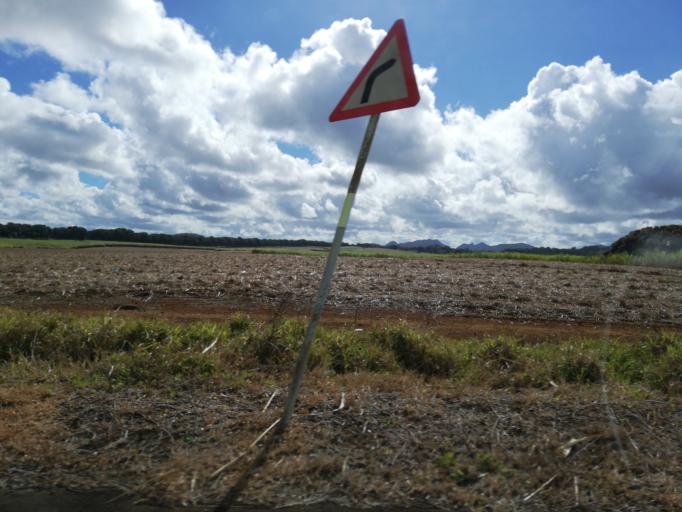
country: MU
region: Grand Port
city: Mahebourg
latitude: -20.4039
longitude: 57.6768
